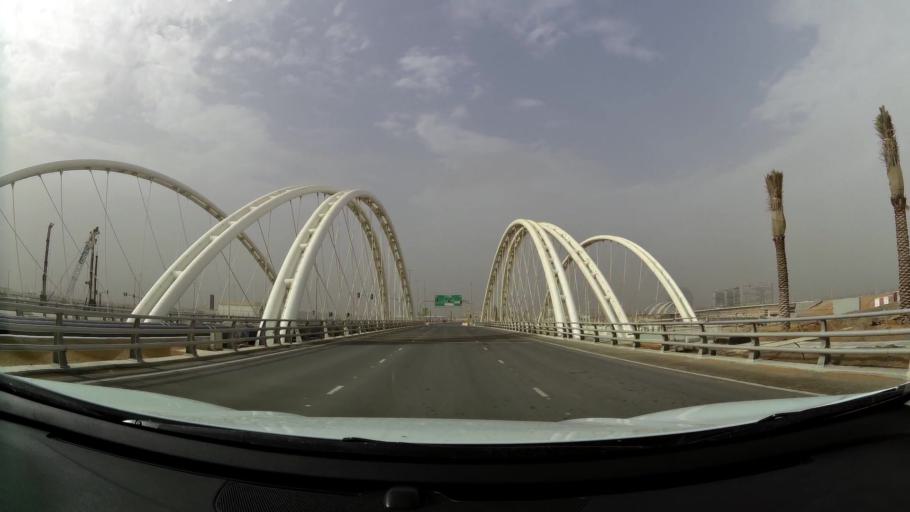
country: AE
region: Abu Dhabi
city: Abu Dhabi
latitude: 24.4467
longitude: 54.5940
